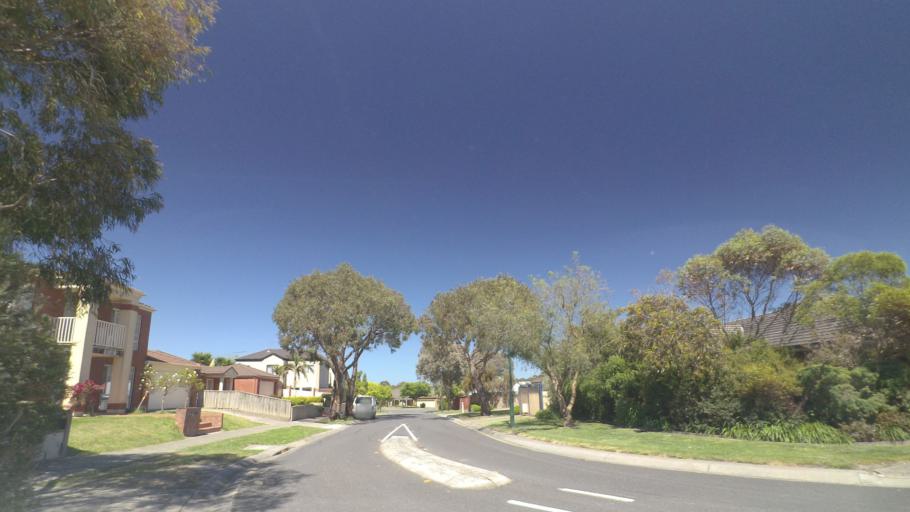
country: AU
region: Victoria
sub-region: Maroondah
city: Croydon Hills
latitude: -37.7892
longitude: 145.2610
